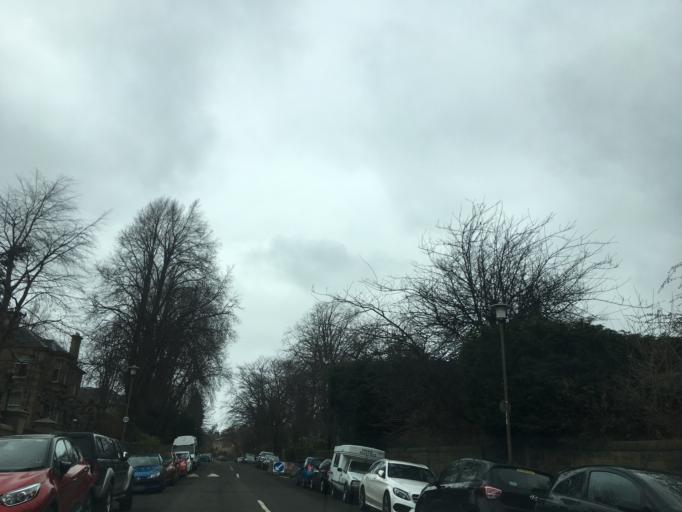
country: GB
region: Scotland
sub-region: Edinburgh
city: Edinburgh
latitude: 55.9307
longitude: -3.1817
